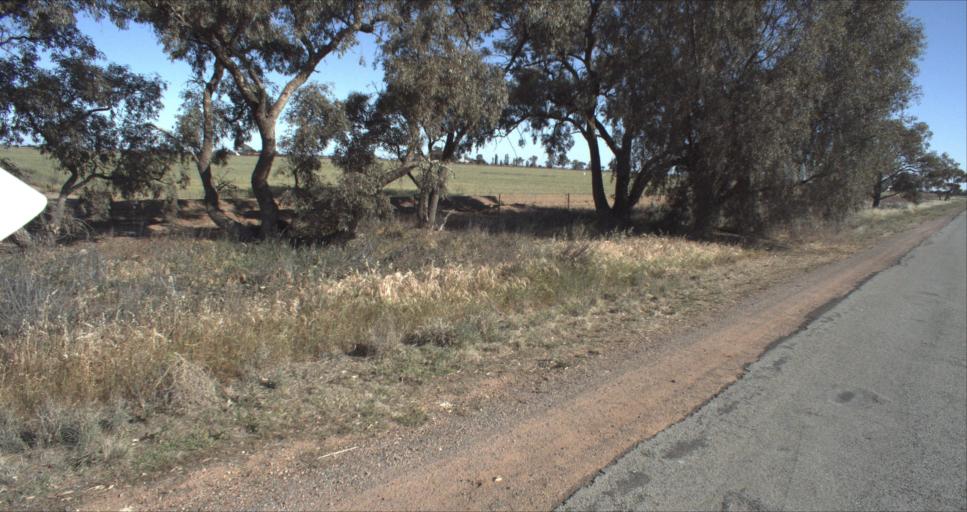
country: AU
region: New South Wales
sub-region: Leeton
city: Leeton
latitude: -34.5562
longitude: 146.3136
